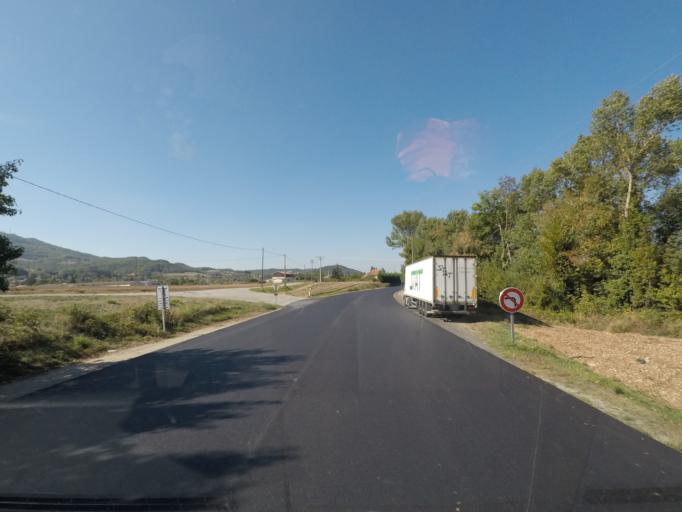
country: FR
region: Rhone-Alpes
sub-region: Departement de la Drome
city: Aouste-sur-Sye
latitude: 44.7038
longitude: 5.1055
